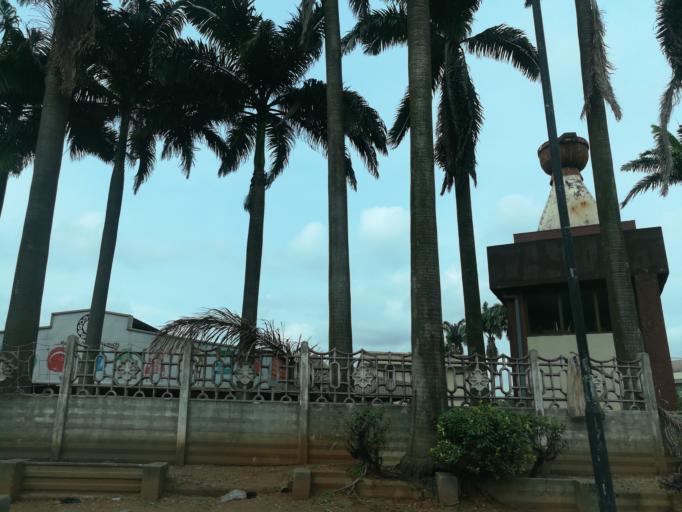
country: NG
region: Lagos
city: Ojota
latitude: 6.6032
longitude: 3.3725
